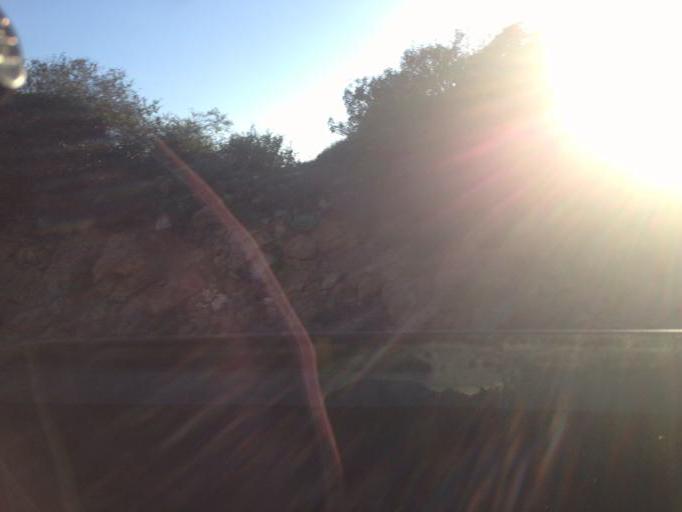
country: MX
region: Baja California
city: El Sauzal
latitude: 31.9057
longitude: -116.7478
